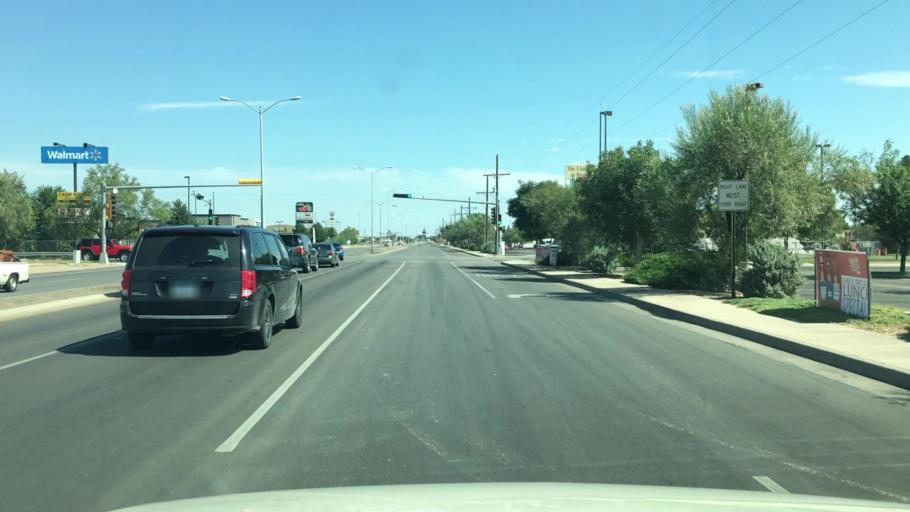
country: US
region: New Mexico
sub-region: Chaves County
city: Roswell
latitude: 33.4480
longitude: -104.5233
